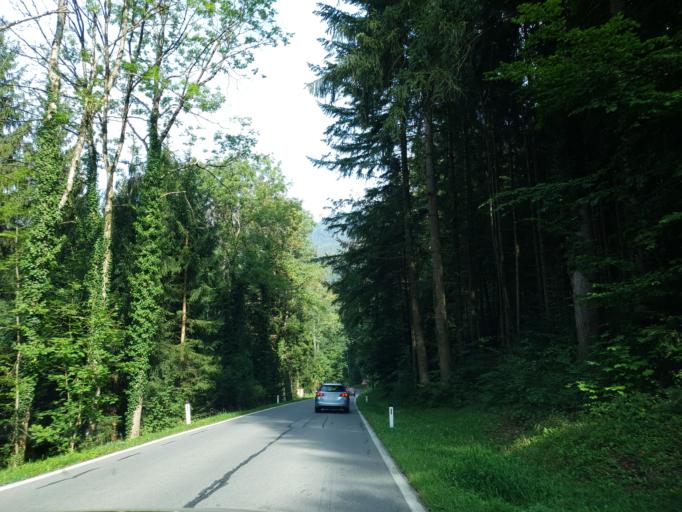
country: AT
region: Vorarlberg
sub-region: Politischer Bezirk Bregenz
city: Bregenz
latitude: 47.4922
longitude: 9.7553
